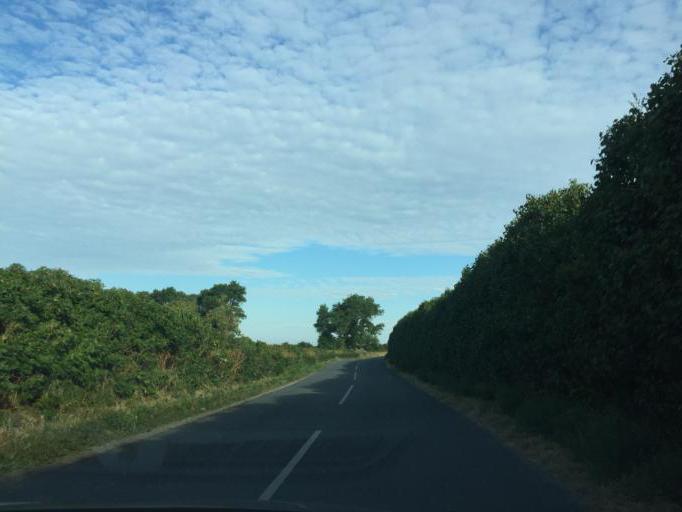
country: DK
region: South Denmark
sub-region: Assens Kommune
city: Harby
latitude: 55.1588
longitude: 9.9967
